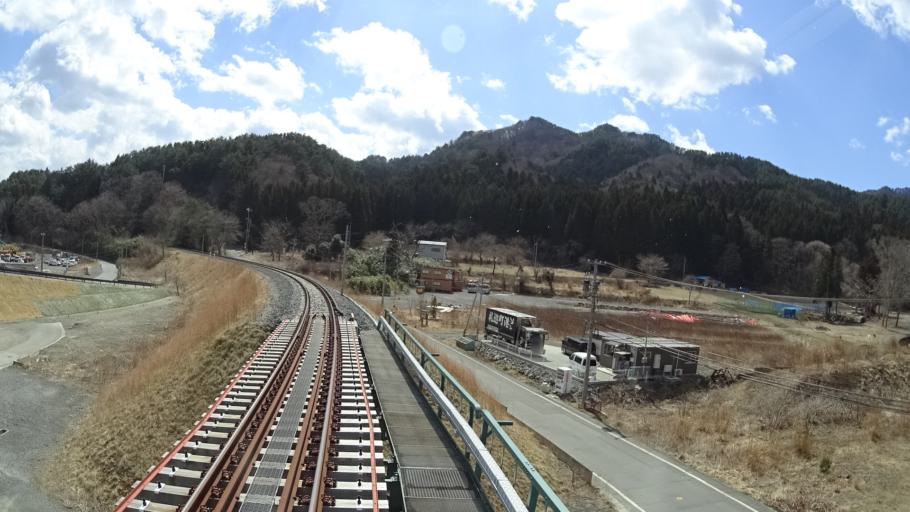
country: JP
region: Iwate
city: Otsuchi
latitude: 39.3827
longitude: 141.9351
